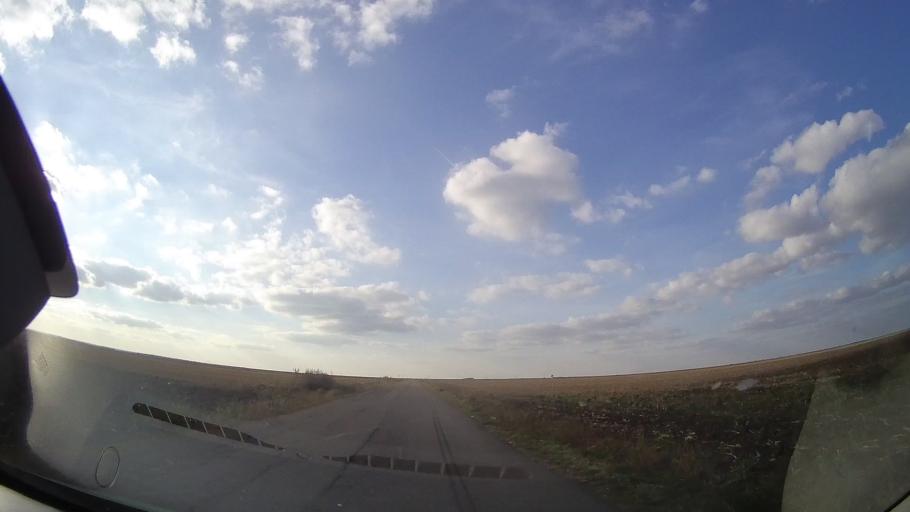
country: RO
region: Constanta
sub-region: Comuna Cerchezu
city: Cerchezu
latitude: 43.8247
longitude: 28.1371
